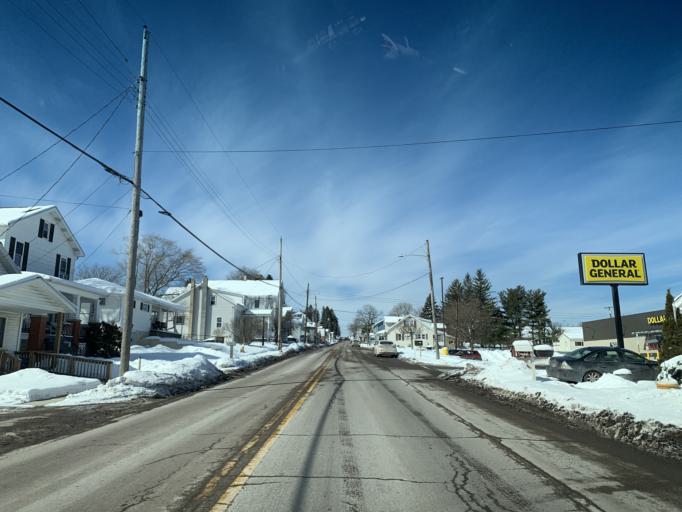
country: US
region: Pennsylvania
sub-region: Somerset County
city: Meyersdale
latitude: 39.6962
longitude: -79.1535
